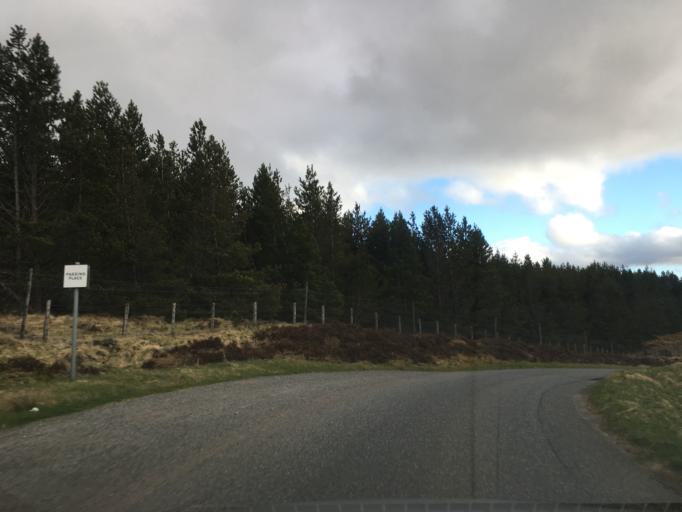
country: GB
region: Scotland
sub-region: Perth and Kinross
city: Aberfeldy
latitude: 56.7750
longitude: -4.0828
